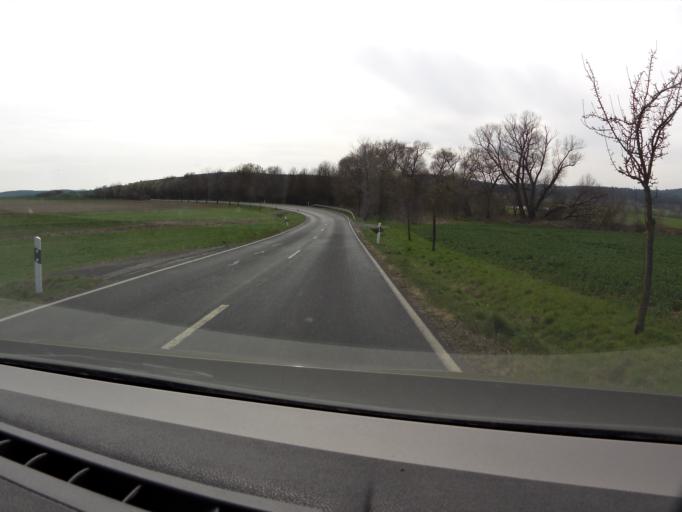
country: DE
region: Thuringia
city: Marksuhl
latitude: 50.8890
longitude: 10.2301
